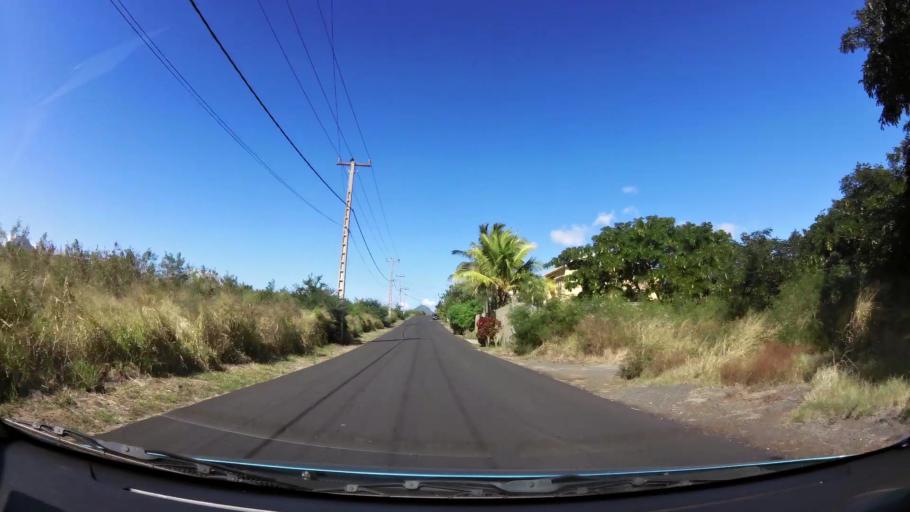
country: MU
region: Black River
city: Flic en Flac
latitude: -20.2678
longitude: 57.3772
